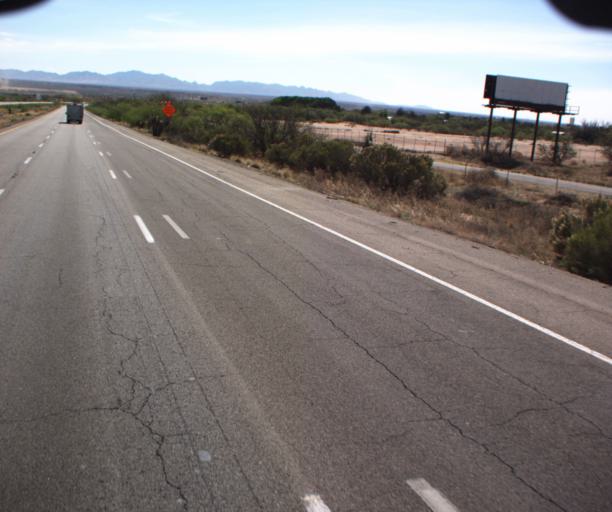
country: US
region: Arizona
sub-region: Cochise County
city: Benson
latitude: 31.9784
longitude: -110.3025
